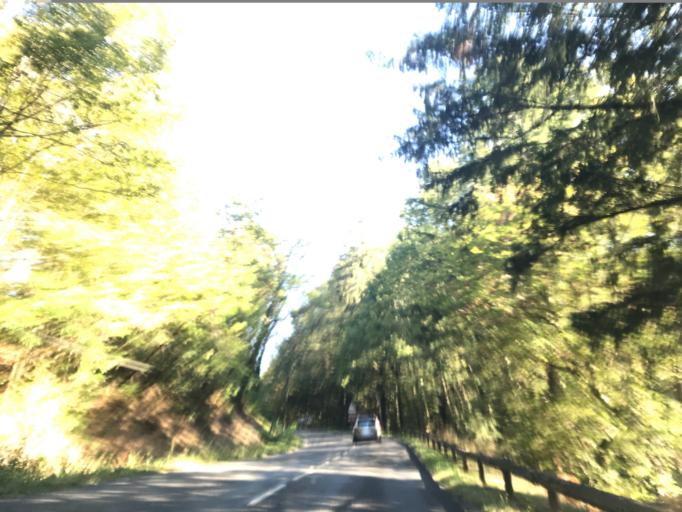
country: FR
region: Auvergne
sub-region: Departement du Puy-de-Dome
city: Courpiere
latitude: 45.7758
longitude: 3.4991
